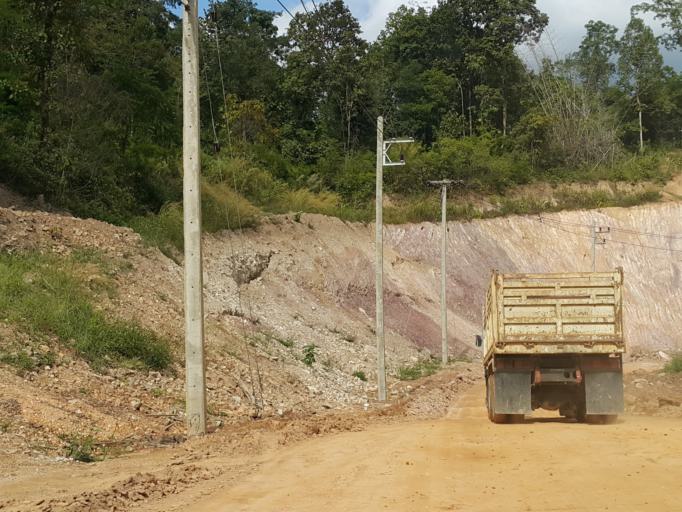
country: TH
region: Lampang
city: Chae Hom
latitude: 18.5757
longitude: 99.4373
